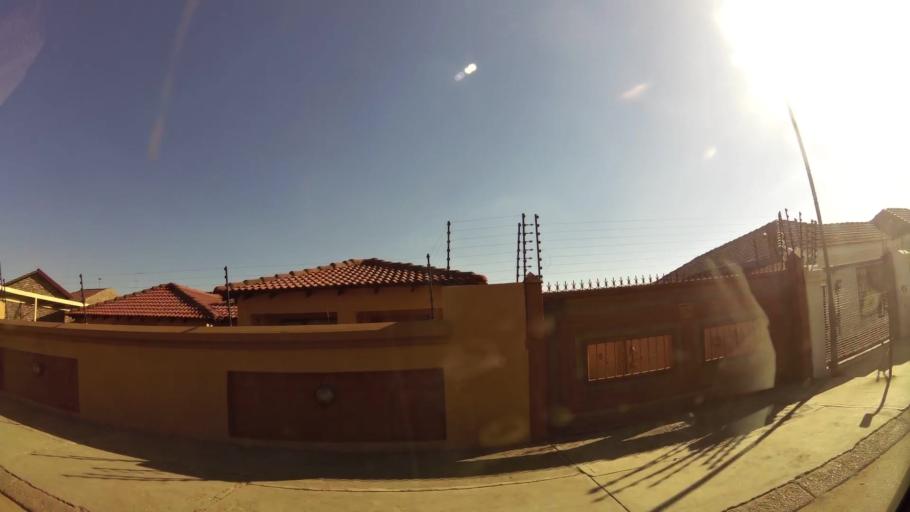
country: ZA
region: Gauteng
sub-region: City of Tshwane Metropolitan Municipality
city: Cullinan
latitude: -25.7173
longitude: 28.3775
